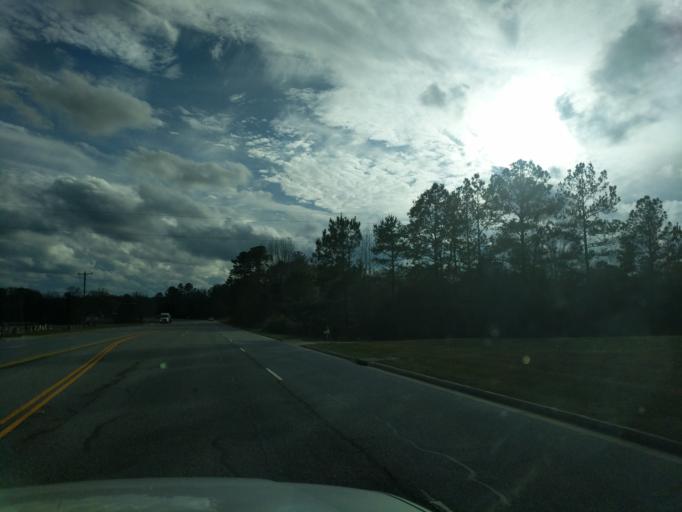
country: US
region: South Carolina
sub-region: Greenwood County
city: Ware Shoals
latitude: 34.4488
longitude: -82.2510
